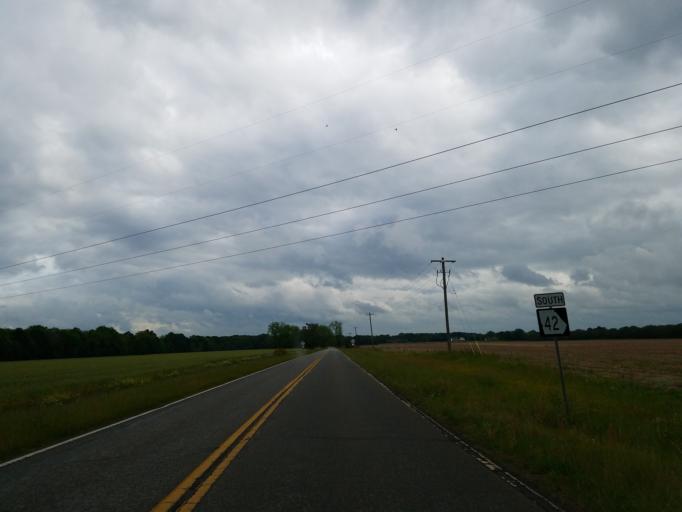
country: US
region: Georgia
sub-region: Peach County
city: Byron
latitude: 32.6630
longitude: -83.8065
